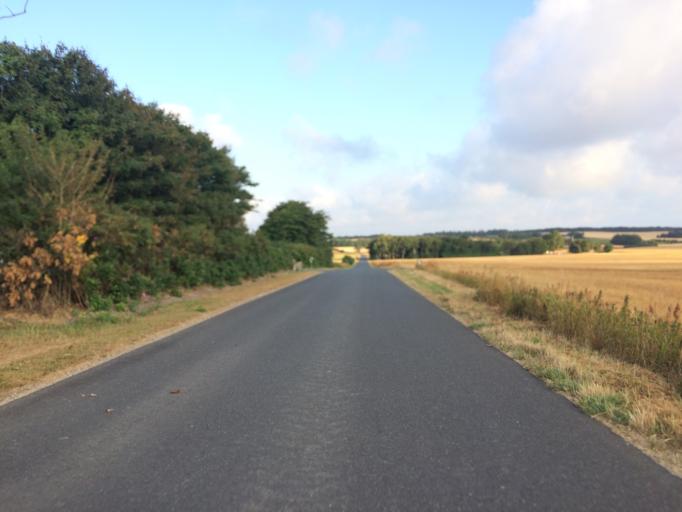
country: DK
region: Central Jutland
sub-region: Holstebro Kommune
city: Vinderup
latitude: 56.6016
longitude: 8.7228
